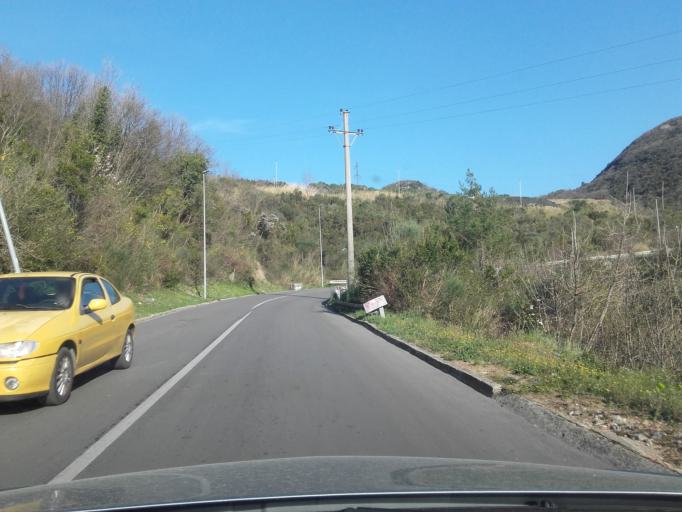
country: ME
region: Budva
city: Budva
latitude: 42.2906
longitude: 18.8250
